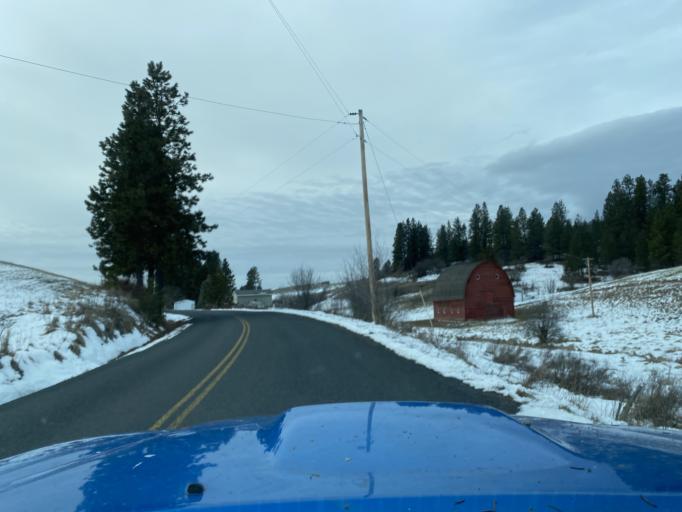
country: US
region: Idaho
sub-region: Latah County
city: Moscow
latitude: 46.6929
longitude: -116.9142
